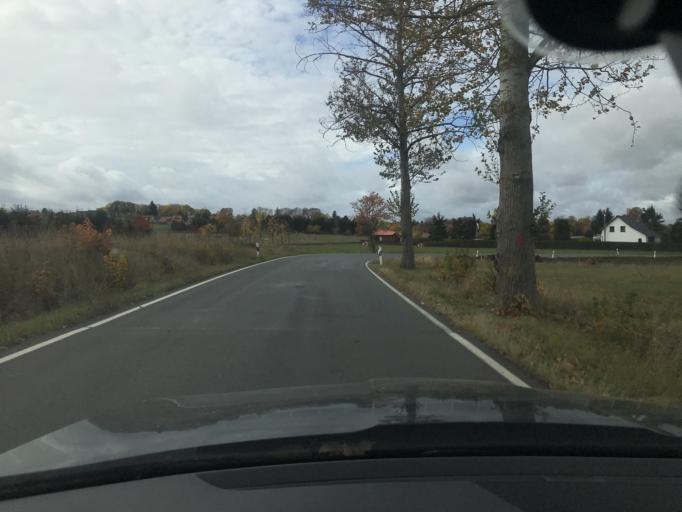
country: DE
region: Saxony-Anhalt
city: Friedrichsbrunn
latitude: 51.6788
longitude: 10.9763
